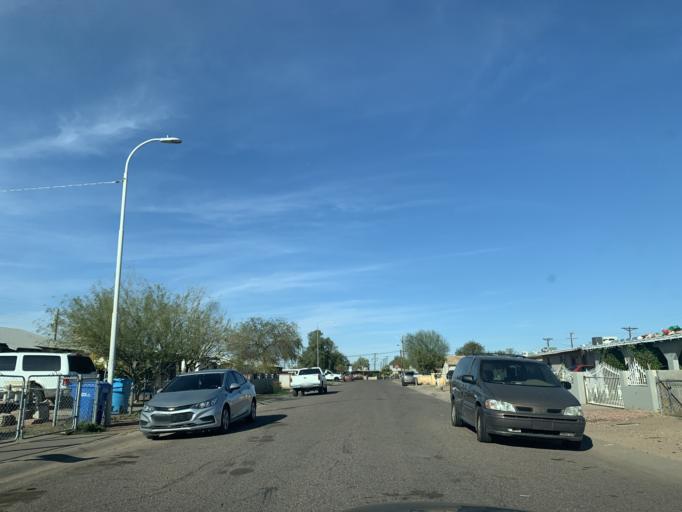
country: US
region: Arizona
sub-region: Maricopa County
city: Laveen
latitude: 33.4019
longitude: -112.1365
